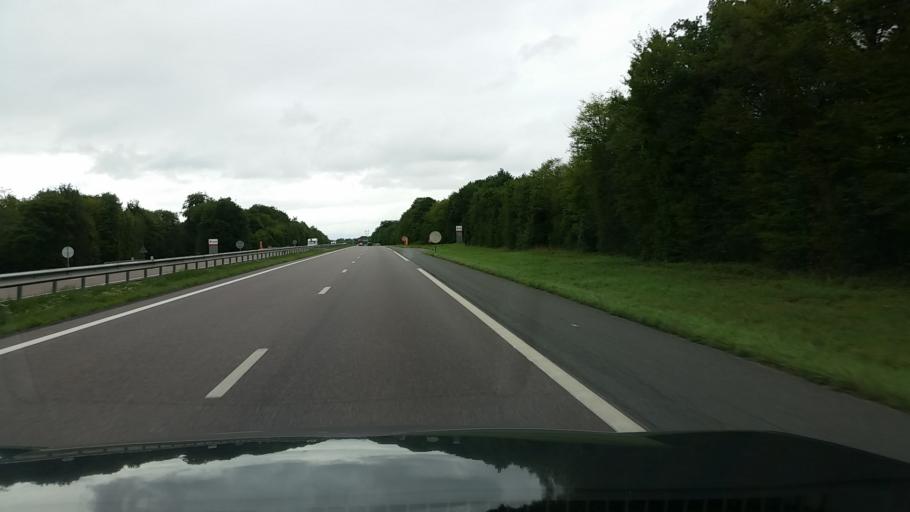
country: FR
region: Lorraine
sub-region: Departement de Meurthe-et-Moselle
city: Colombey-les-Belles
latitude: 48.5071
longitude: 5.9124
